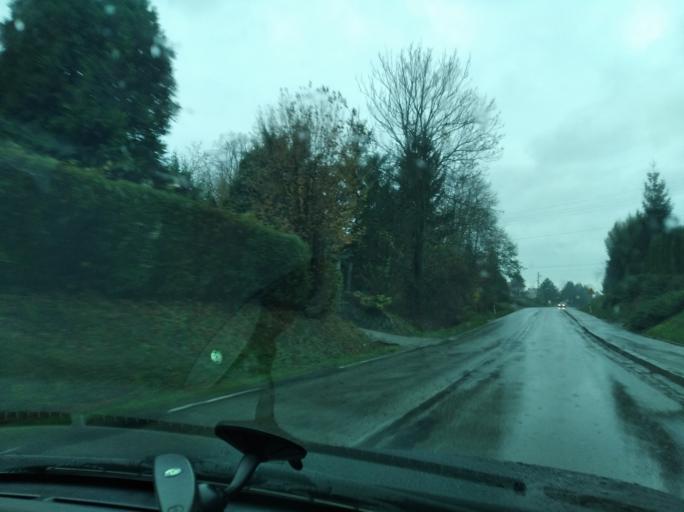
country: PL
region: Subcarpathian Voivodeship
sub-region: Powiat lancucki
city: Albigowa
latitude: 50.0409
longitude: 22.2298
